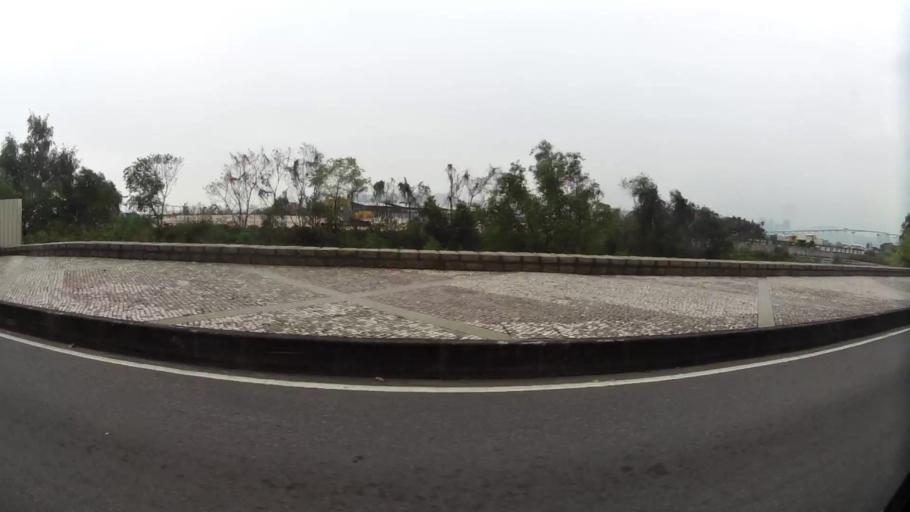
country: MO
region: Macau
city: Macau
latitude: 22.1859
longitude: 113.5497
